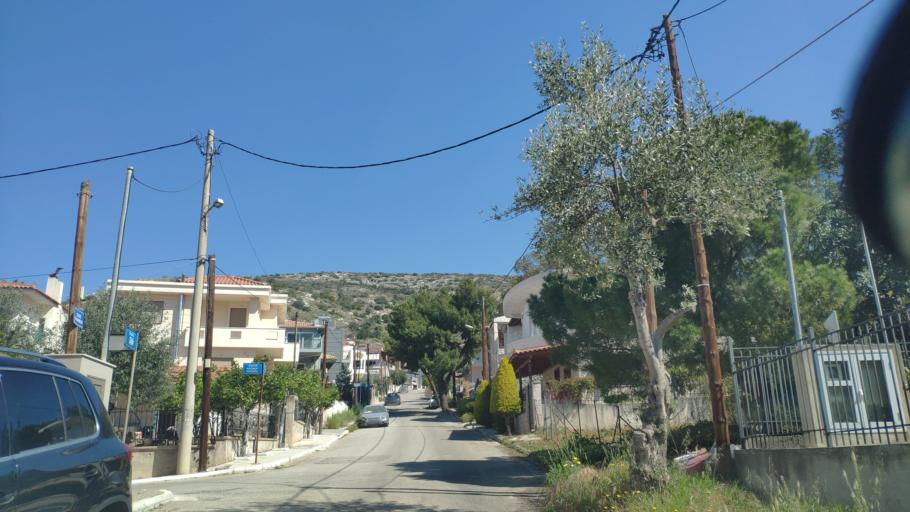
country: GR
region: Attica
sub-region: Nomarchia Athinas
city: Skaramangas
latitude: 38.0133
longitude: 23.6154
